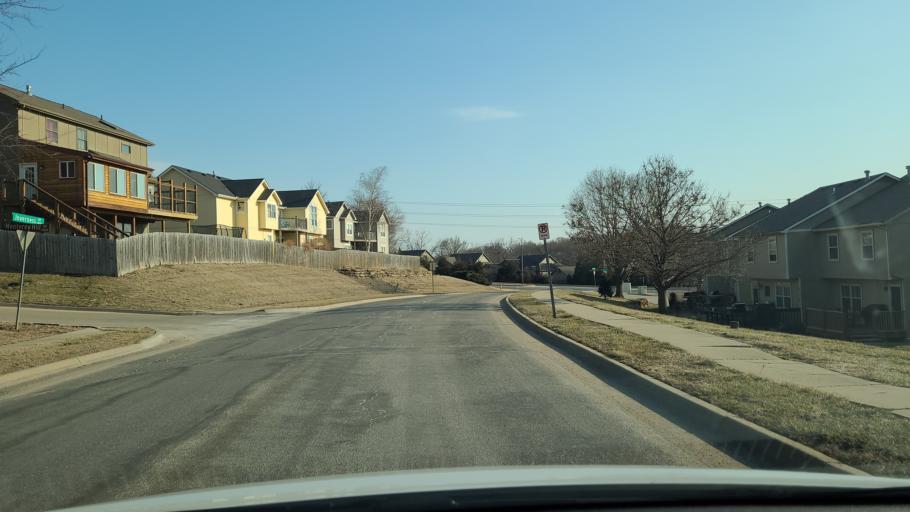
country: US
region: Kansas
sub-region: Douglas County
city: Lawrence
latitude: 38.9581
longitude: -95.2987
